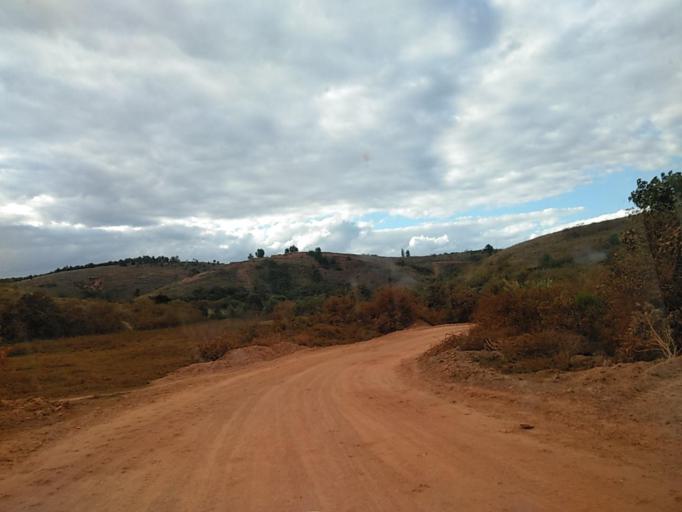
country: MG
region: Alaotra Mangoro
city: Ambatondrazaka
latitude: -18.0209
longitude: 48.2559
